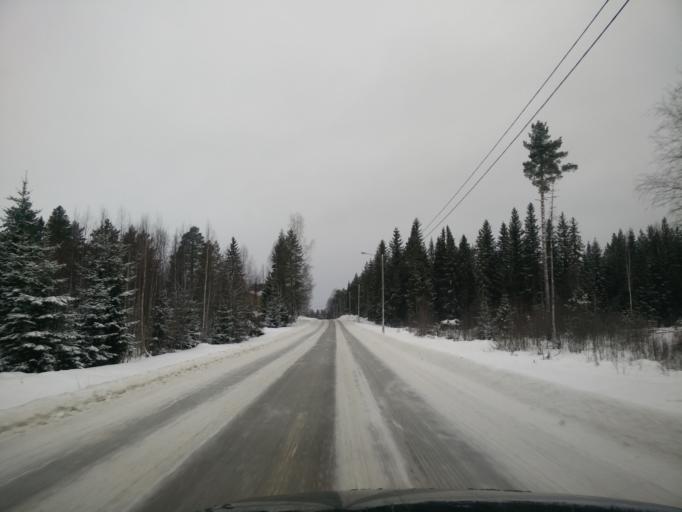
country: SE
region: Jaemtland
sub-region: Braecke Kommun
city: Braecke
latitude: 62.3959
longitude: 15.2193
